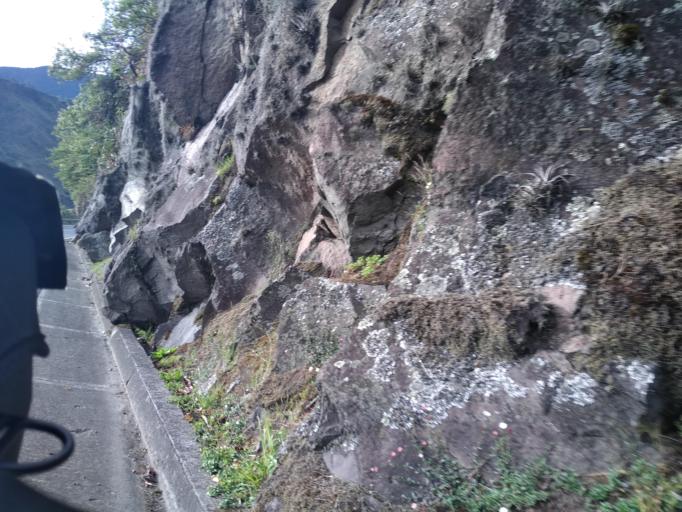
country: CO
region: Narino
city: Funes
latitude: 0.9470
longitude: -77.4736
